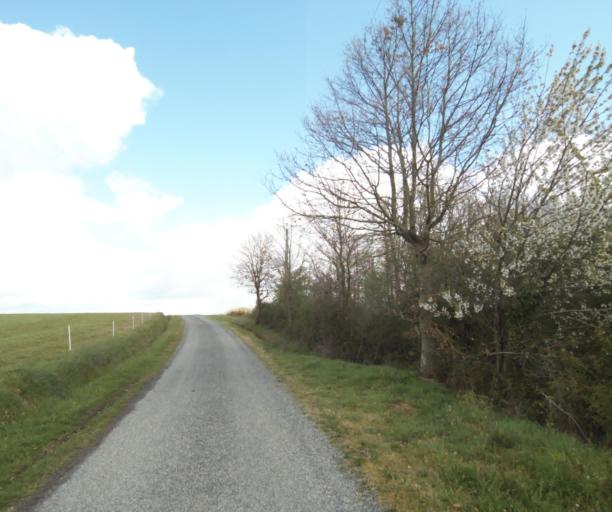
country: FR
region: Midi-Pyrenees
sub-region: Departement de l'Ariege
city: Saverdun
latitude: 43.1802
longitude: 1.5788
